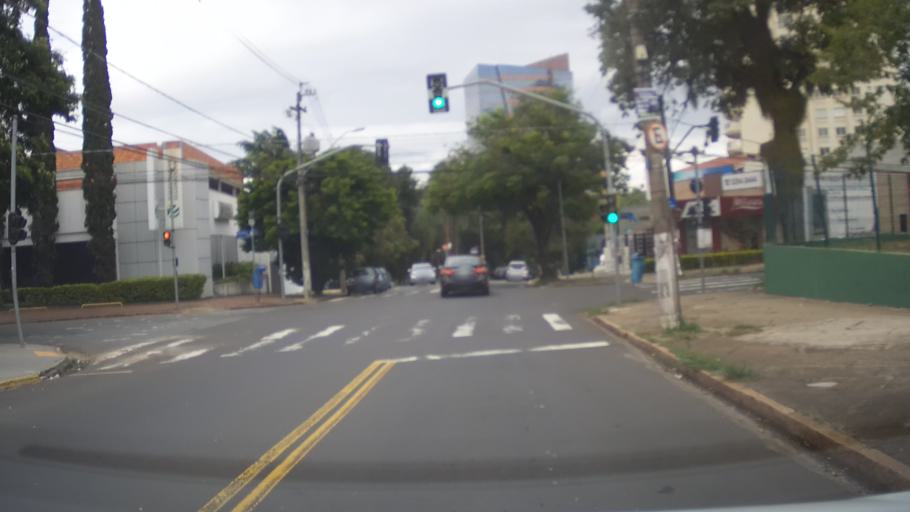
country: BR
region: Sao Paulo
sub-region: Campinas
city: Campinas
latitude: -22.8936
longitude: -47.0503
